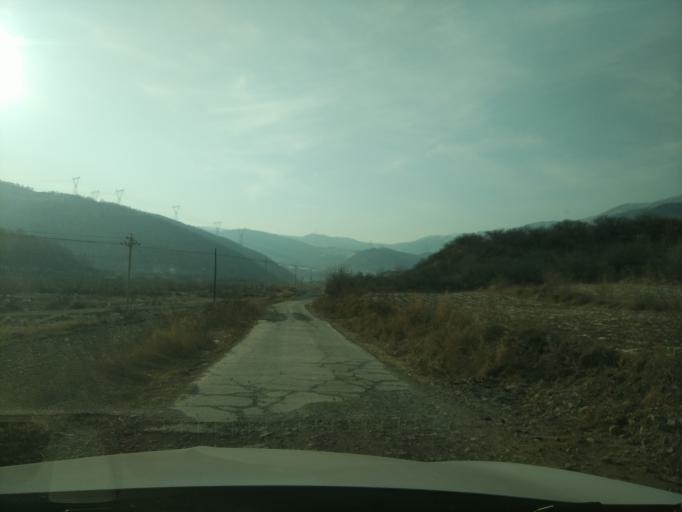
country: CN
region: Hebei
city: Xiwanzi
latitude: 40.8177
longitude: 115.4756
